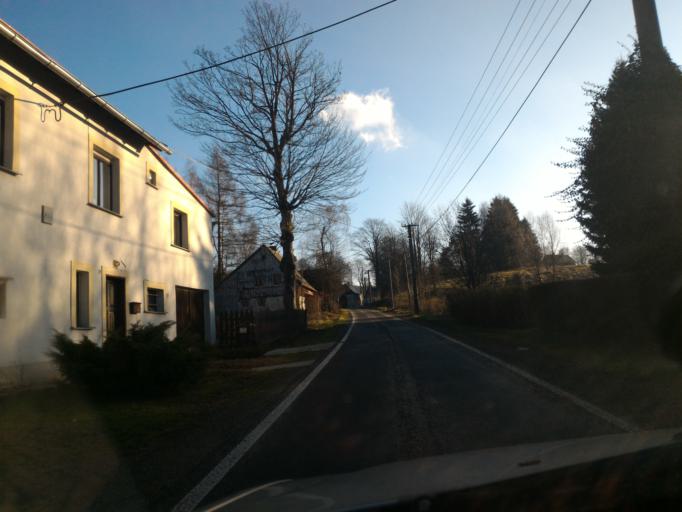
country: DE
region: Saxony
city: Kurort Jonsdorf
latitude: 50.8367
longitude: 14.7072
